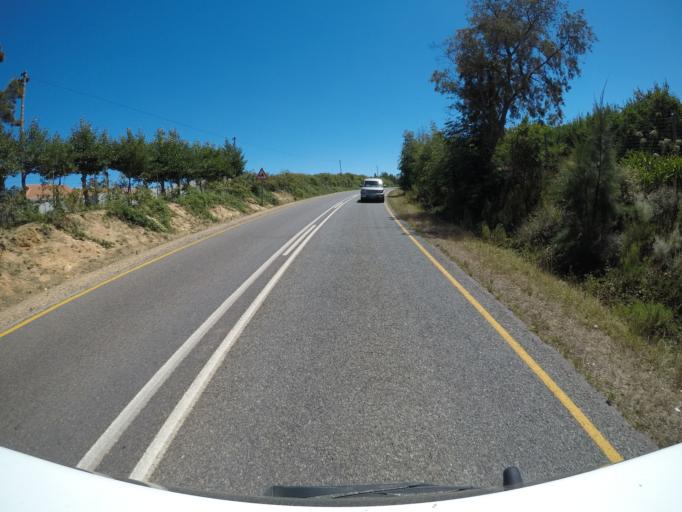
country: ZA
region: Western Cape
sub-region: Overberg District Municipality
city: Grabouw
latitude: -34.2131
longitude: 19.0519
